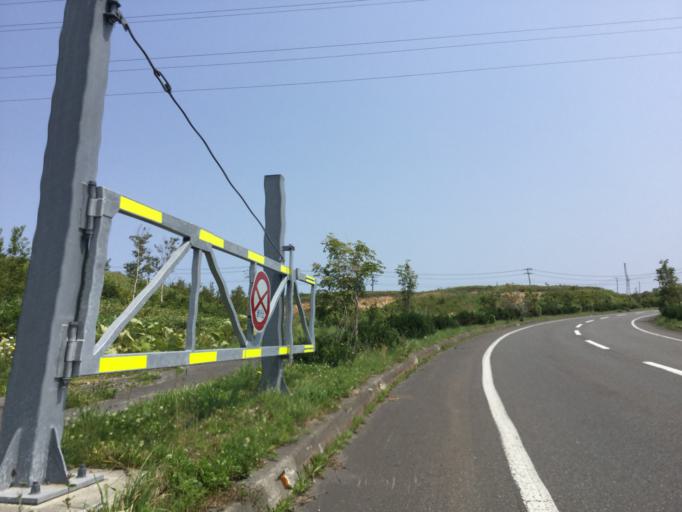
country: JP
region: Hokkaido
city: Wakkanai
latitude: 45.3859
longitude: 141.7247
